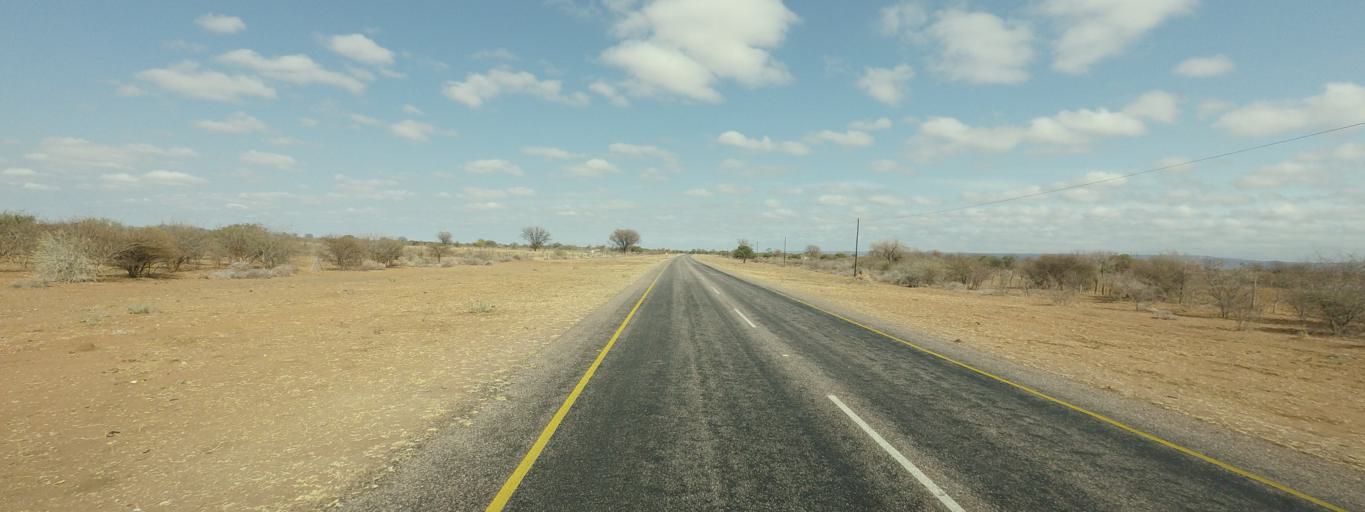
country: BW
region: Central
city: Ratholo
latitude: -22.8098
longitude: 27.5334
